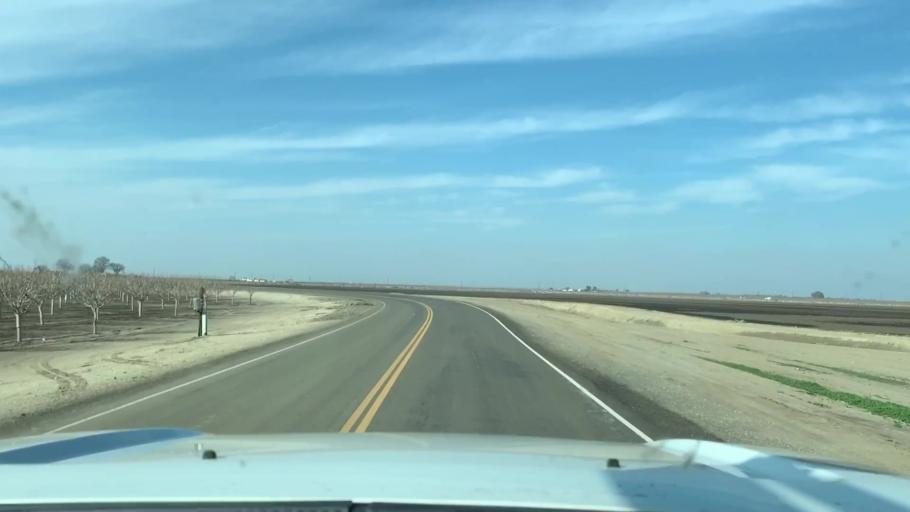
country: US
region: California
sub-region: Kern County
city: Buttonwillow
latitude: 35.4518
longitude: -119.5613
